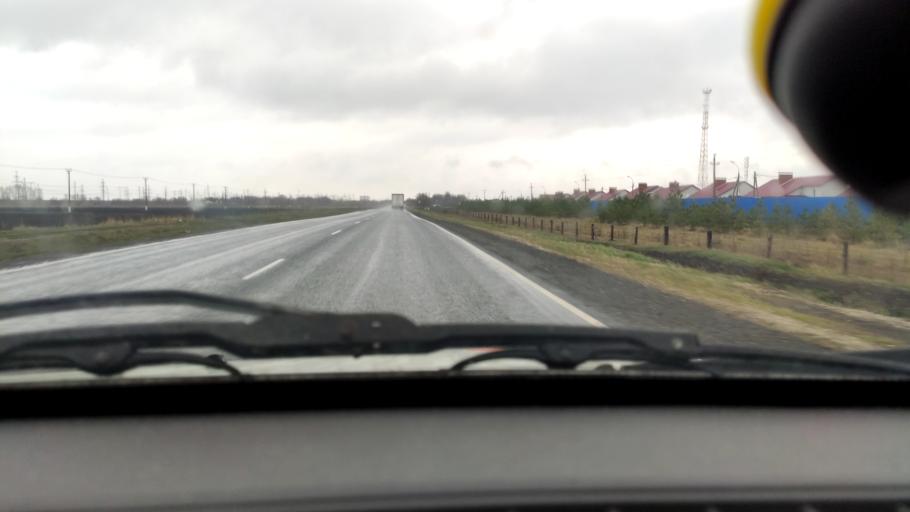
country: RU
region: Samara
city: Povolzhskiy
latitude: 53.6459
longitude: 49.6729
